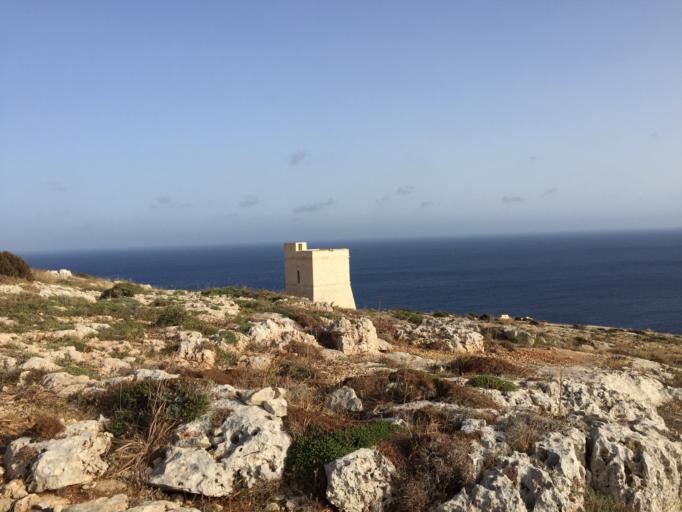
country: MT
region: Il-Qrendi
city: Qrendi
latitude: 35.8254
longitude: 14.4396
